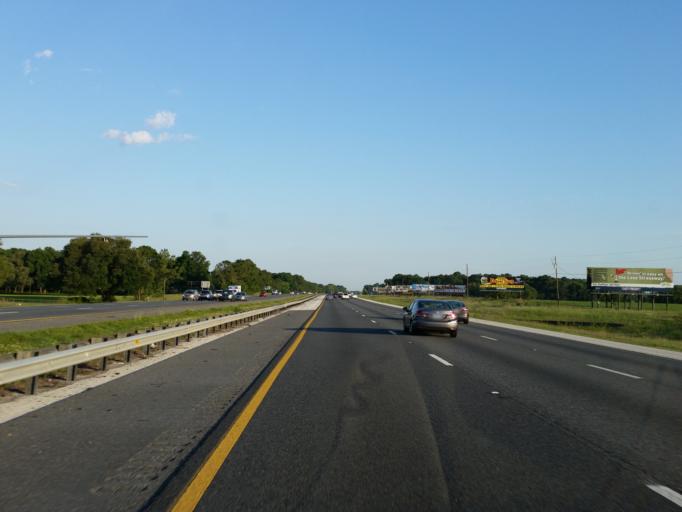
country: US
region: Florida
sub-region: Marion County
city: Belleview
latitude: 28.9737
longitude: -82.1315
